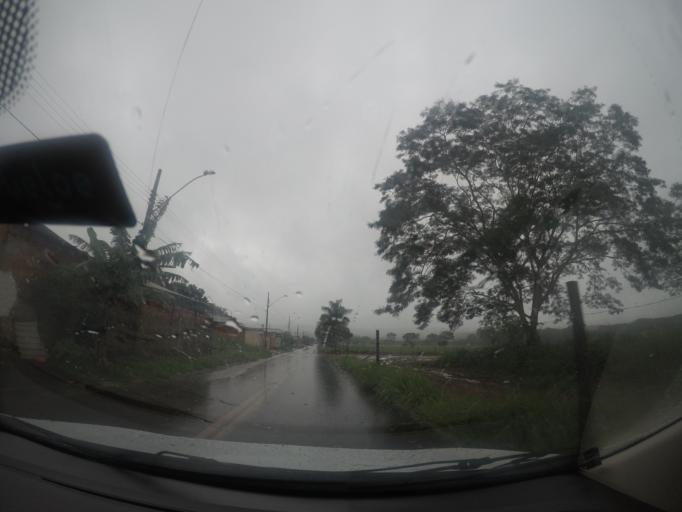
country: BR
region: Goias
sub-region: Goianira
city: Goianira
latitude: -16.5901
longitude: -49.3461
